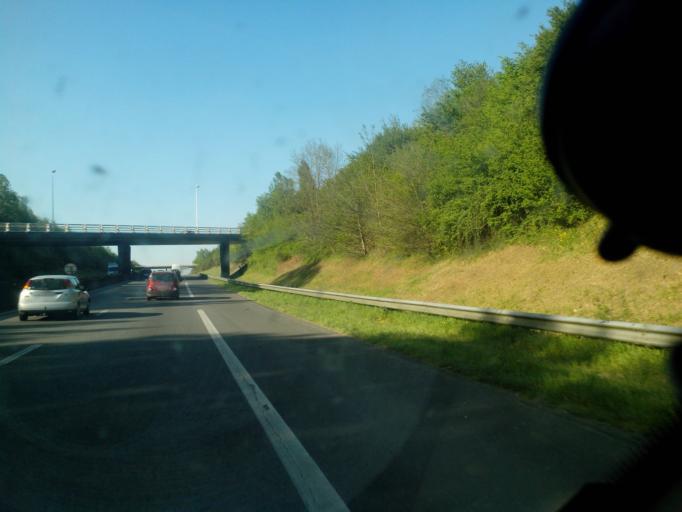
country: FR
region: Pays de la Loire
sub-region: Departement de la Loire-Atlantique
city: Orvault
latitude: 47.2413
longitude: -1.6231
